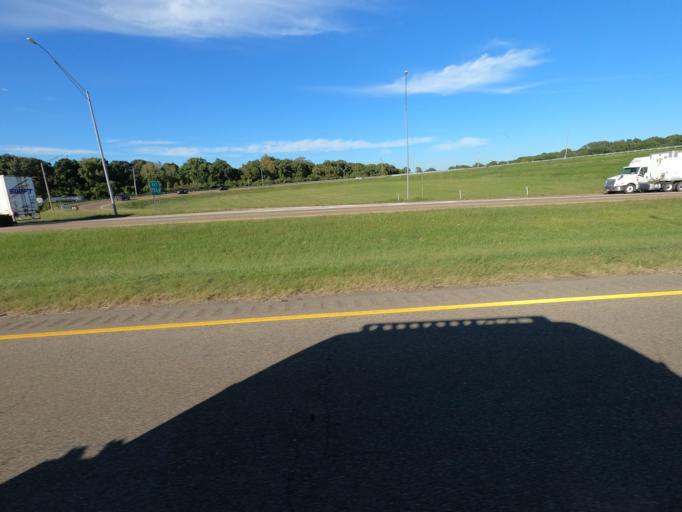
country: US
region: Tennessee
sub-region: Shelby County
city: New South Memphis
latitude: 35.0729
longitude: -90.0291
